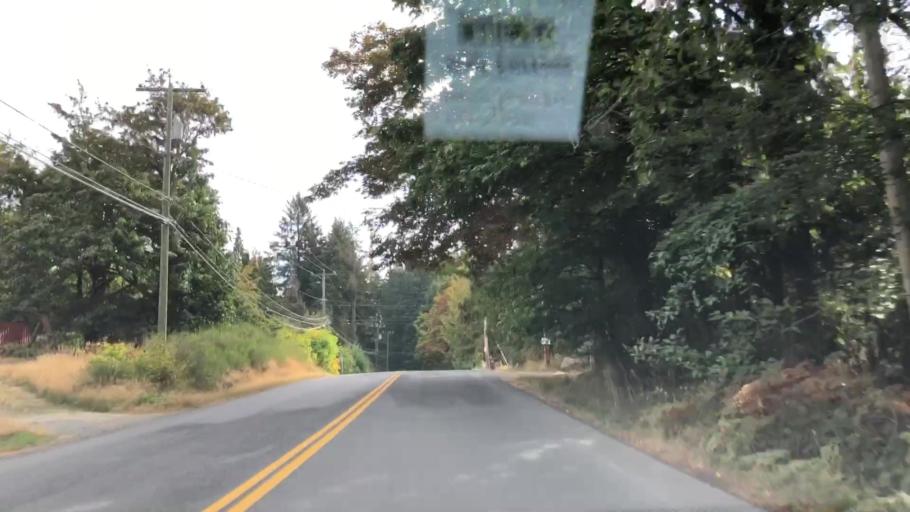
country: CA
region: British Columbia
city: North Saanich
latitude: 48.6865
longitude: -123.5751
